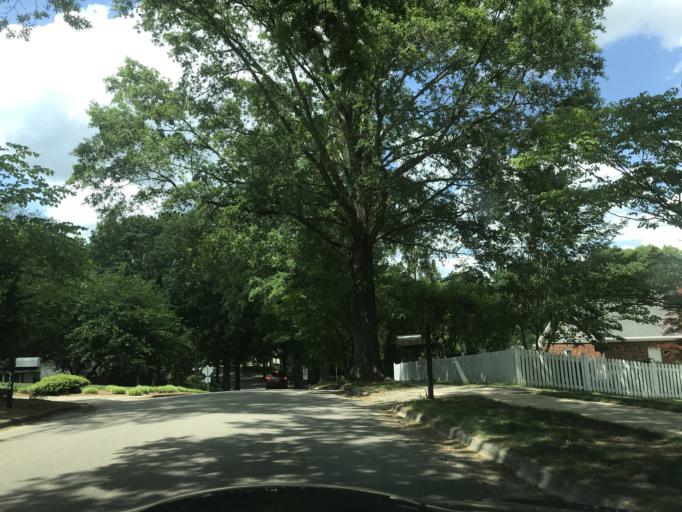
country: US
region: North Carolina
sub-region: Wake County
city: West Raleigh
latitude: 35.8529
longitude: -78.6304
